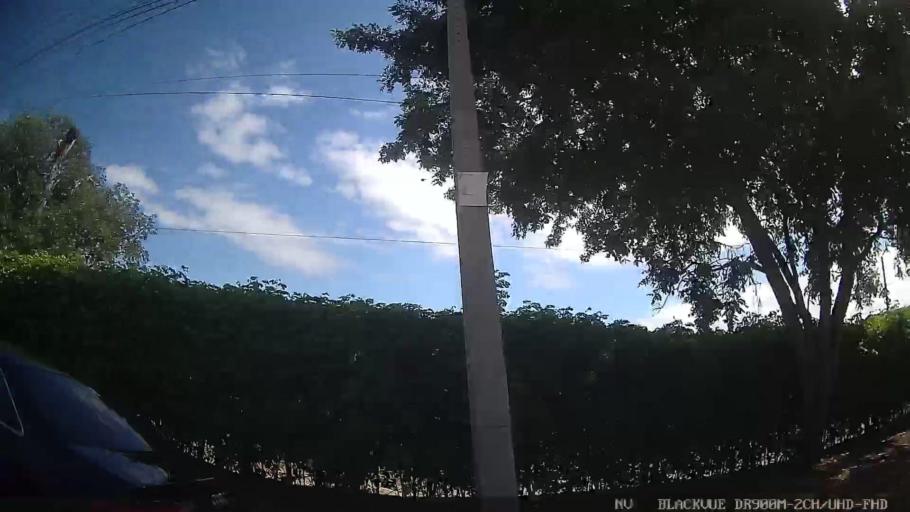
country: BR
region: Sao Paulo
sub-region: Jarinu
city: Jarinu
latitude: -23.0733
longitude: -46.6588
